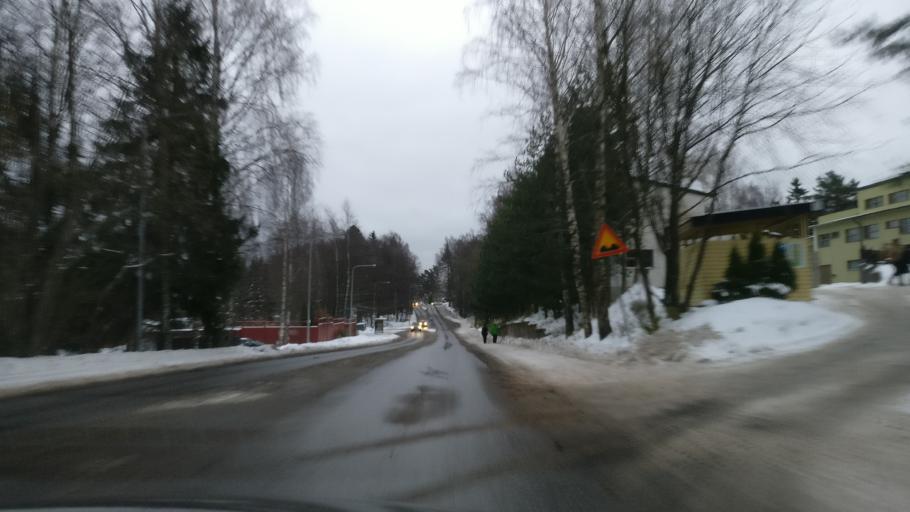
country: FI
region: Uusimaa
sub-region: Helsinki
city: Helsinki
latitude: 60.1669
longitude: 25.0520
